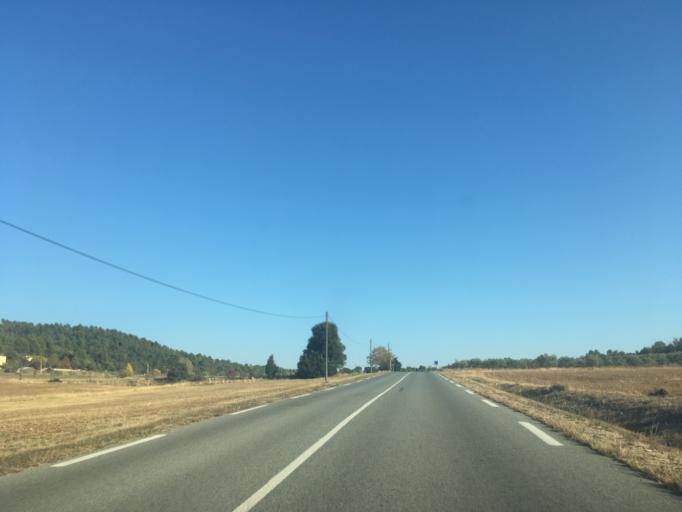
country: FR
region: Provence-Alpes-Cote d'Azur
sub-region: Departement du Var
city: Aups
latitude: 43.6001
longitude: 6.2426
